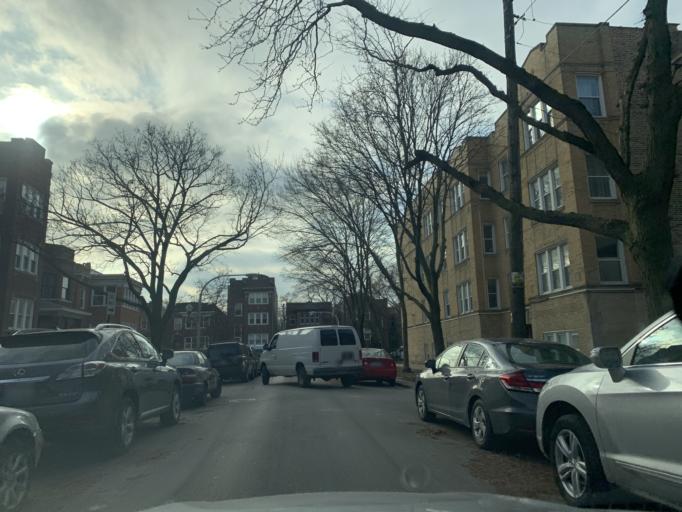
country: US
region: Illinois
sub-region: Cook County
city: Lincolnwood
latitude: 41.9674
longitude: -87.6963
